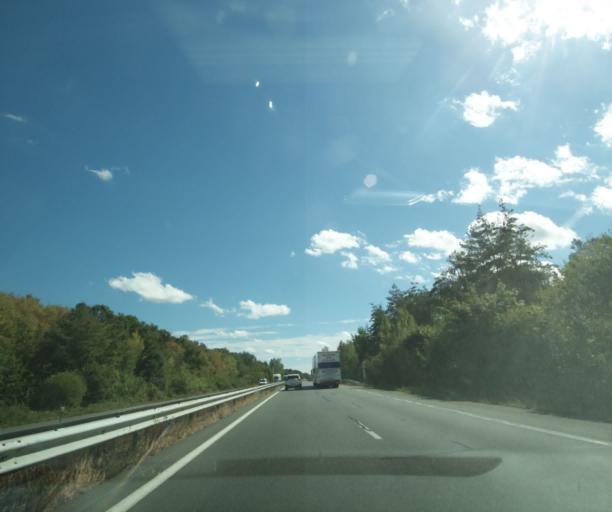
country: FR
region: Aquitaine
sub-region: Departement du Lot-et-Garonne
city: Fourques-sur-Garonne
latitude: 44.4139
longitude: 0.1786
